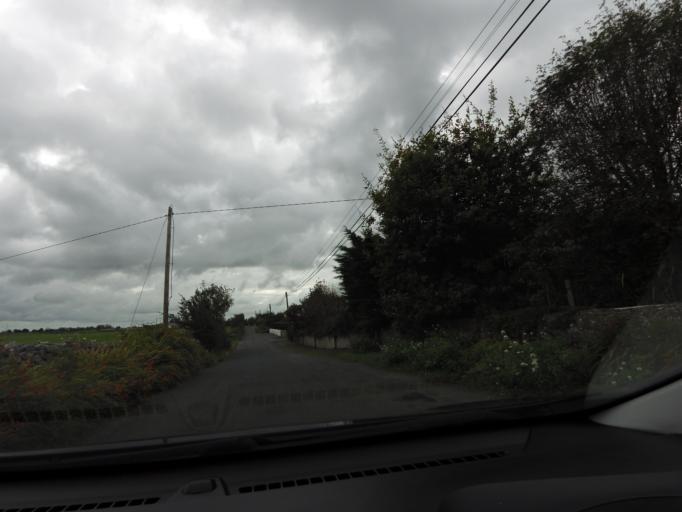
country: IE
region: Connaught
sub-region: County Galway
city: Athenry
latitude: 53.3204
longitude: -8.7804
